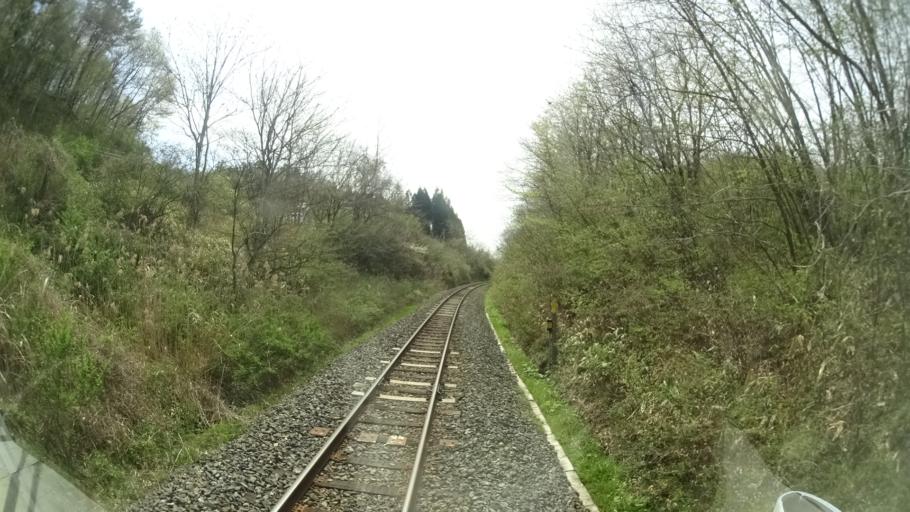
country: JP
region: Iwate
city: Ichinoseki
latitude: 38.9688
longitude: 141.3315
